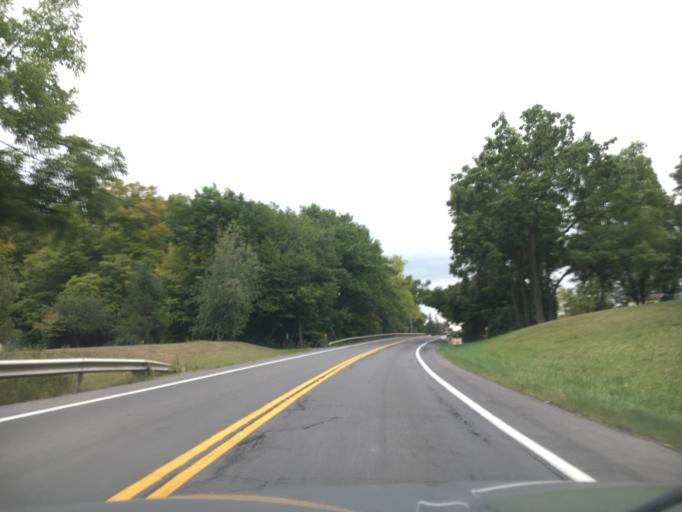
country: US
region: New York
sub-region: Tompkins County
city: Trumansburg
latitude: 42.6684
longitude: -76.7297
